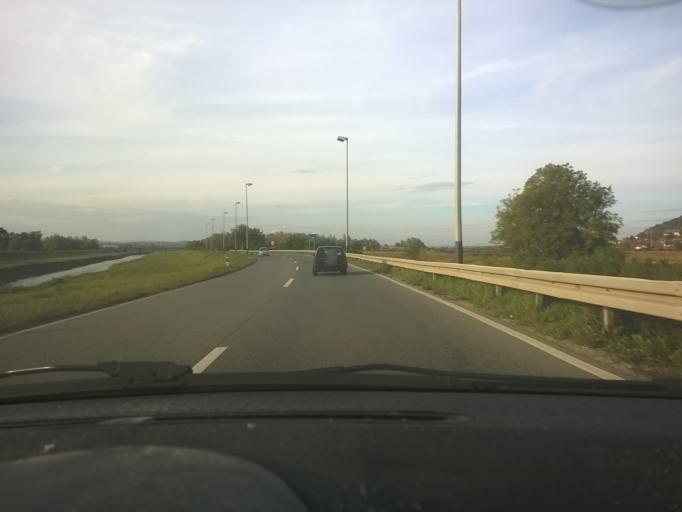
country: HR
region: Zagrebacka
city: Zapresic
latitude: 45.8440
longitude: 15.8299
